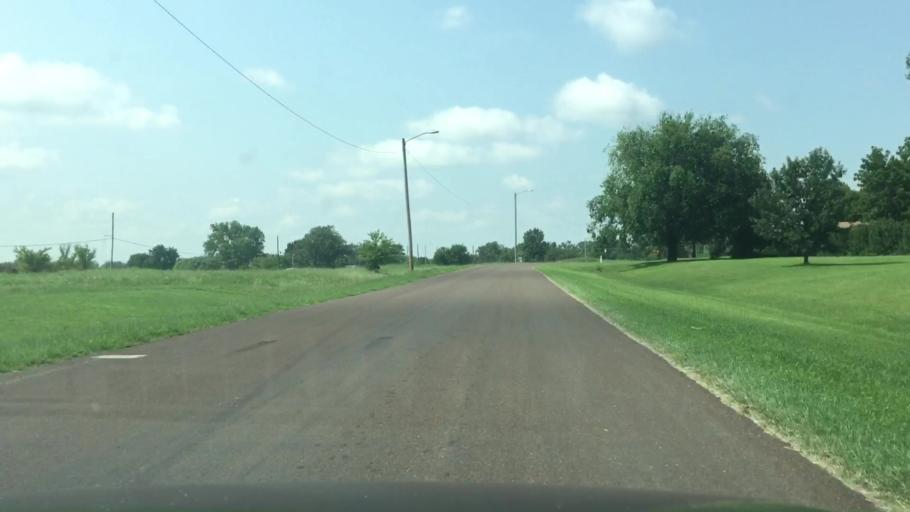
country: US
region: Kansas
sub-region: Allen County
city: Iola
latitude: 37.9051
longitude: -95.4066
